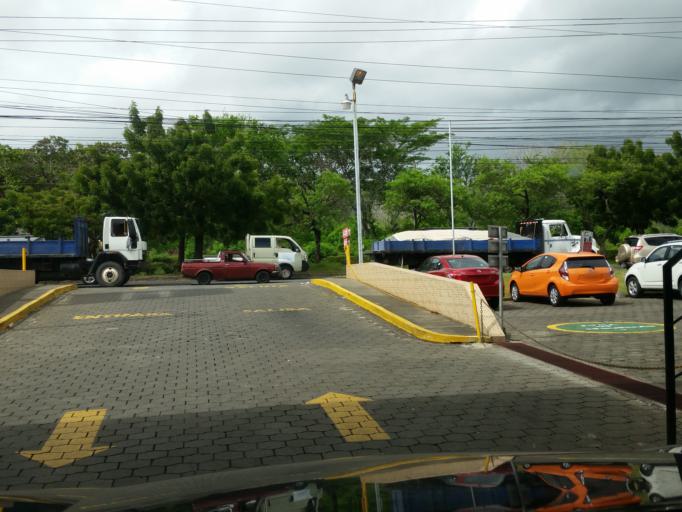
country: NI
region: Managua
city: Managua
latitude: 12.1132
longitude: -86.2612
